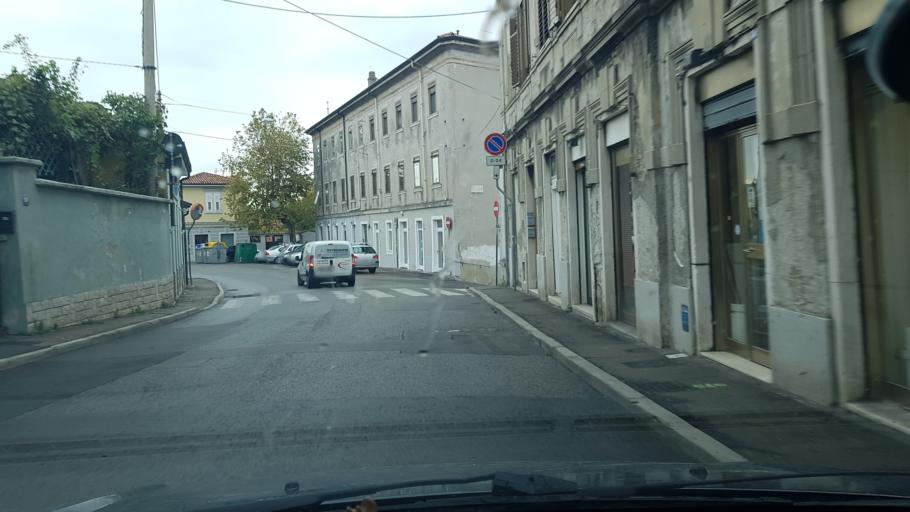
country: IT
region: Friuli Venezia Giulia
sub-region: Provincia di Trieste
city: Trieste
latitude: 45.6246
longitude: 13.7847
